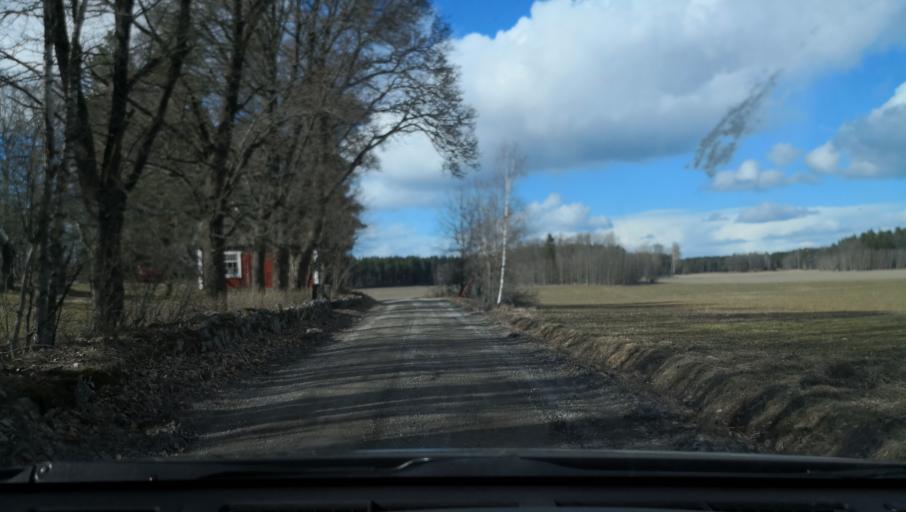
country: SE
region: OErebro
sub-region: Lindesbergs Kommun
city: Fellingsbro
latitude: 59.4233
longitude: 15.6916
